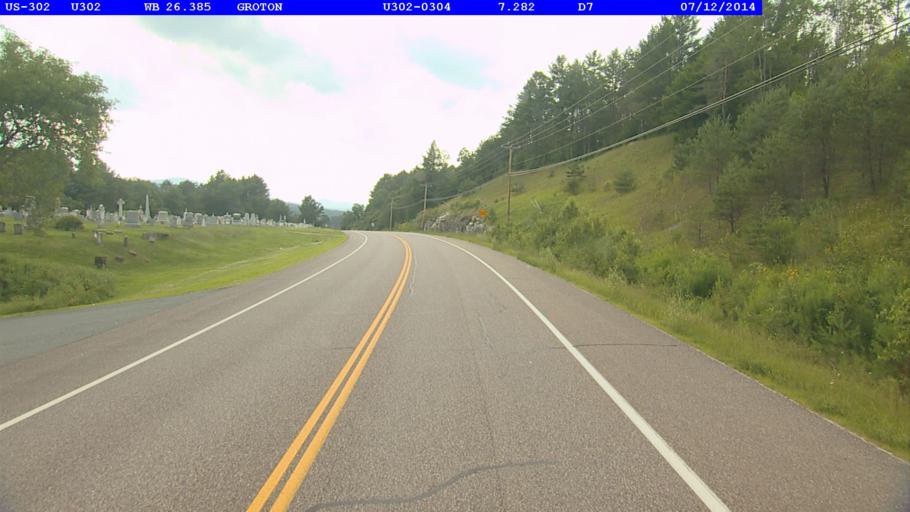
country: US
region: New Hampshire
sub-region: Grafton County
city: Woodsville
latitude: 44.2065
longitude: -72.1817
